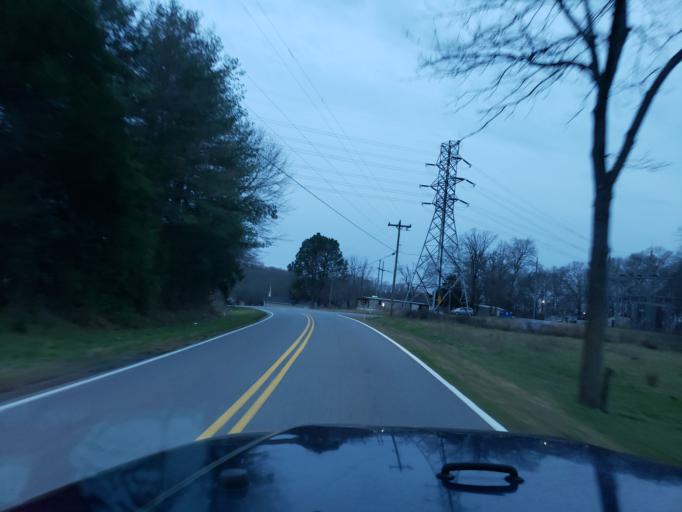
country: US
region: North Carolina
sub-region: Cleveland County
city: White Plains
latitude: 35.2469
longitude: -81.4594
